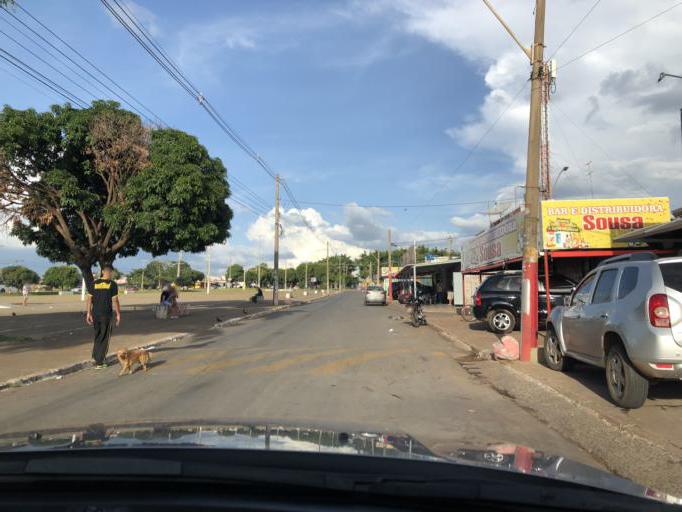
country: BR
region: Federal District
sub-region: Brasilia
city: Brasilia
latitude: -15.8061
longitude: -48.1356
